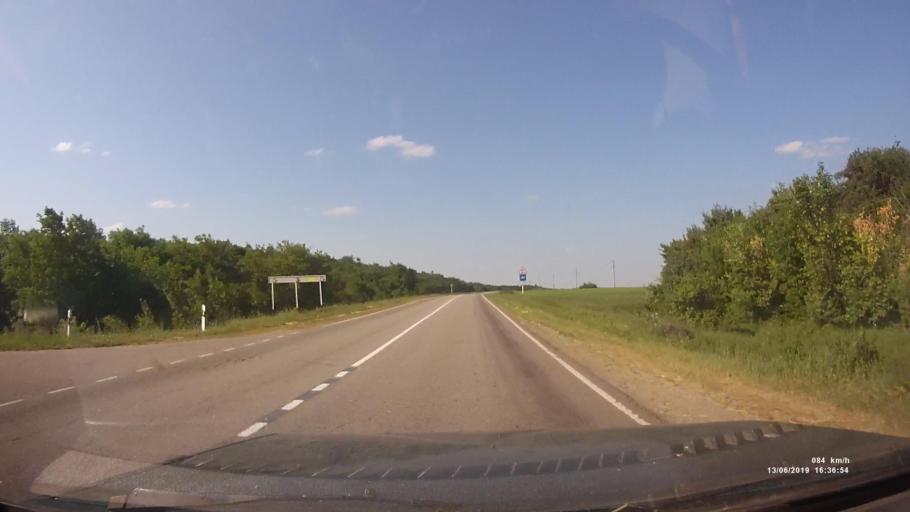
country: RU
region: Rostov
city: Kazanskaya
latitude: 49.9007
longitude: 41.3088
